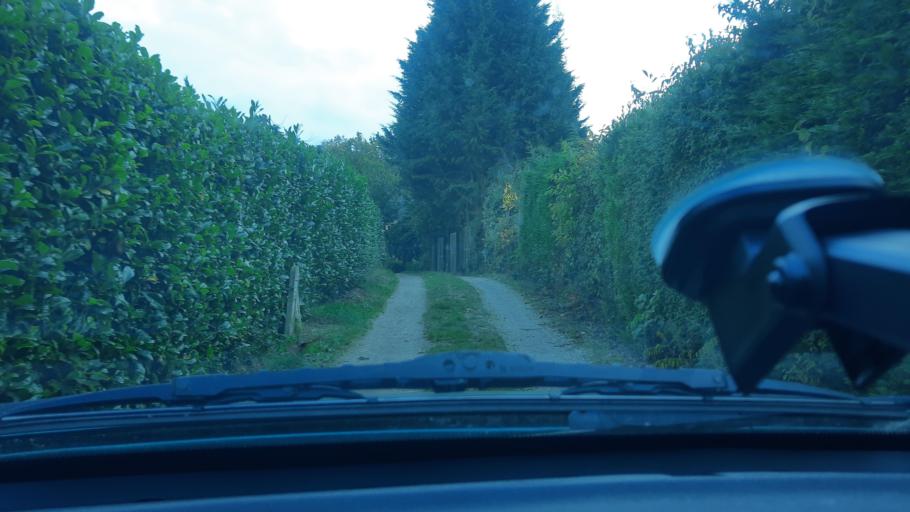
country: NL
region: North Brabant
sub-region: Gemeente Boxmeer
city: Boxmeer
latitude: 51.6539
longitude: 5.9948
